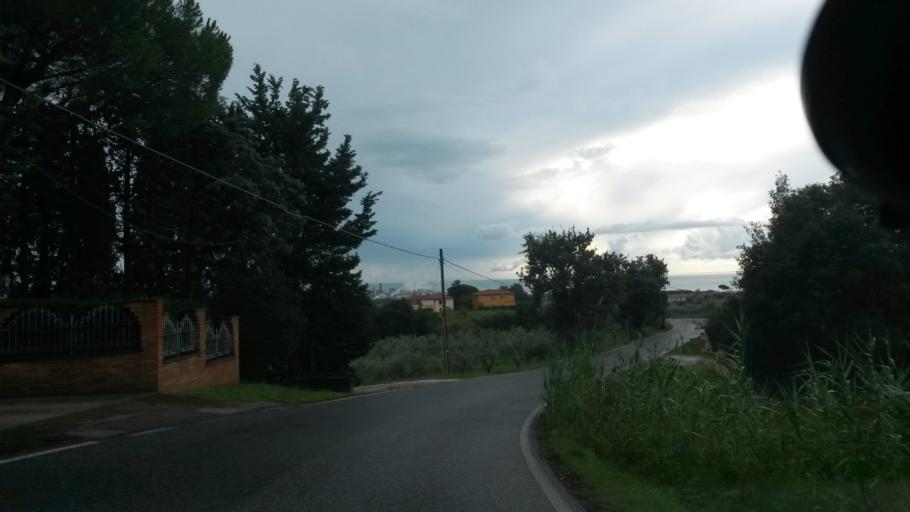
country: IT
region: Tuscany
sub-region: Provincia di Livorno
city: Rosignano Solvay-Castiglioncello
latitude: 43.4074
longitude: 10.4484
